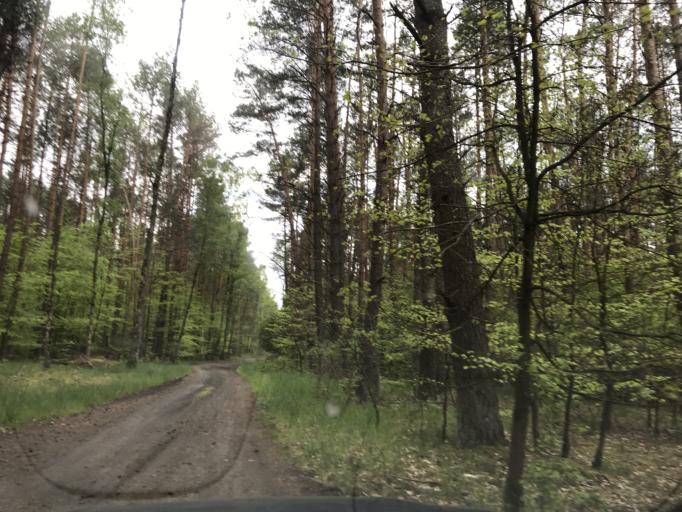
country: PL
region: West Pomeranian Voivodeship
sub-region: Powiat mysliborski
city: Mysliborz
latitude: 52.8694
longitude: 14.8843
